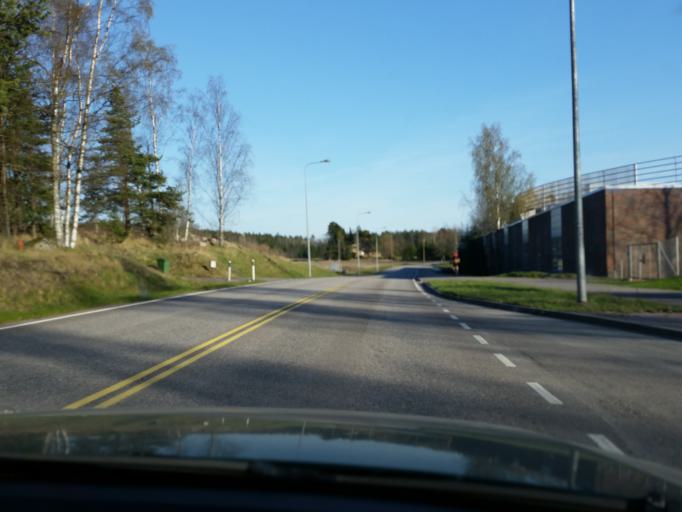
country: FI
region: Uusimaa
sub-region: Helsinki
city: Kirkkonummi
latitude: 60.1319
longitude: 24.5136
